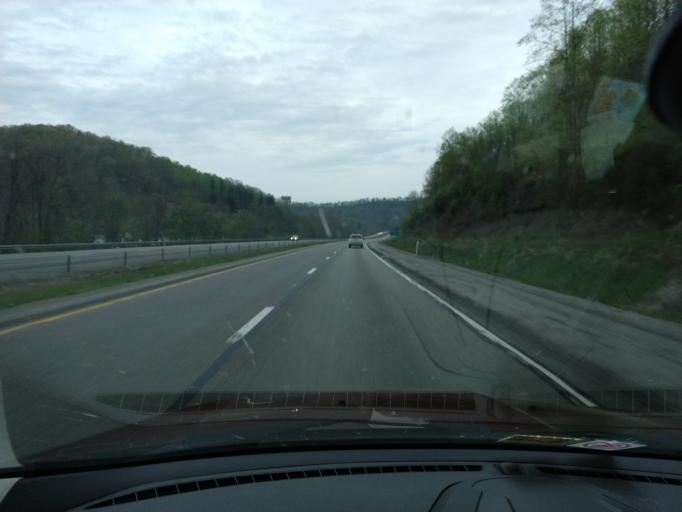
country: US
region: West Virginia
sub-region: Lewis County
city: Weston
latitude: 39.0030
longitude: -80.4997
